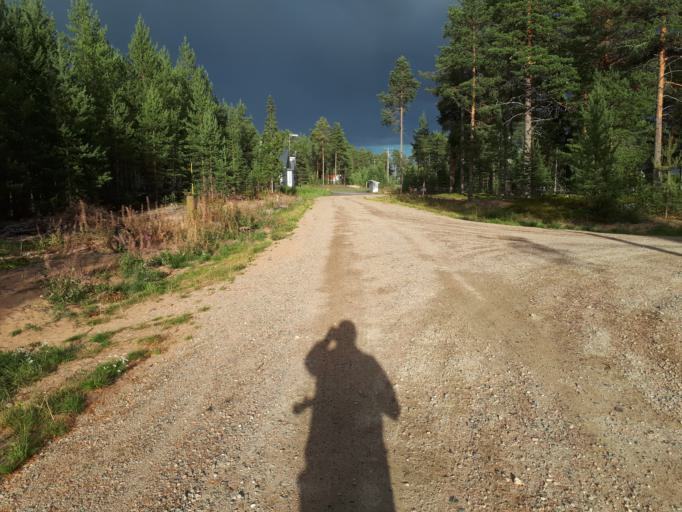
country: FI
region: Northern Ostrobothnia
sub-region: Oulunkaari
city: Ii
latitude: 65.3250
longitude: 25.4026
